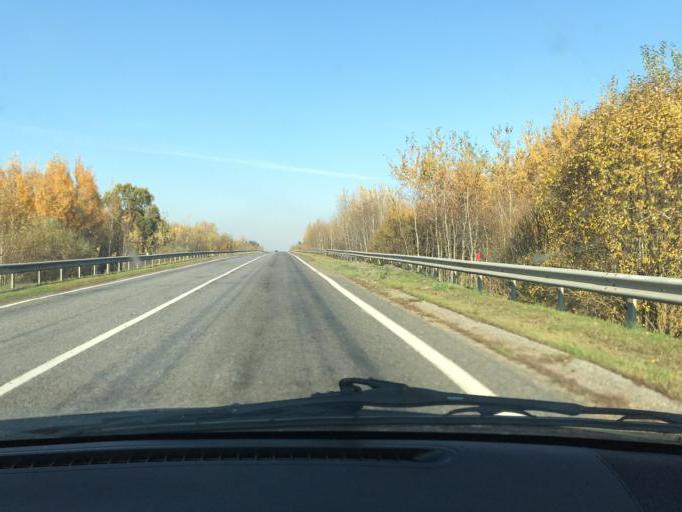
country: BY
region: Vitebsk
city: Orsha
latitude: 54.4300
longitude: 30.4794
